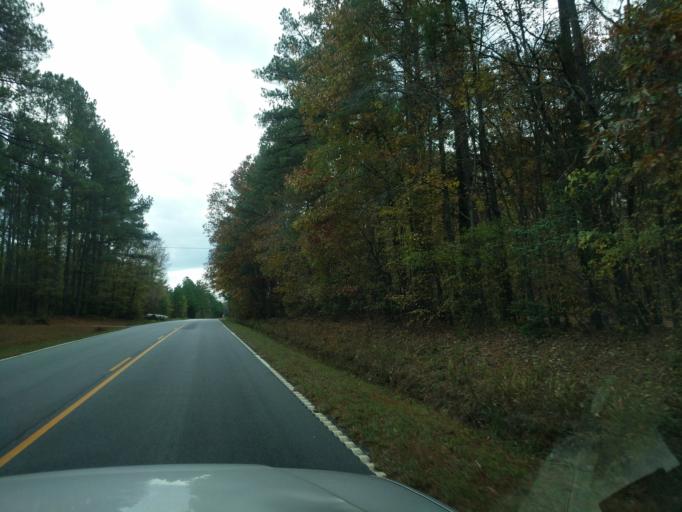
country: US
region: South Carolina
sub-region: Saluda County
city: Saluda
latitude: 34.0666
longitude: -81.8177
